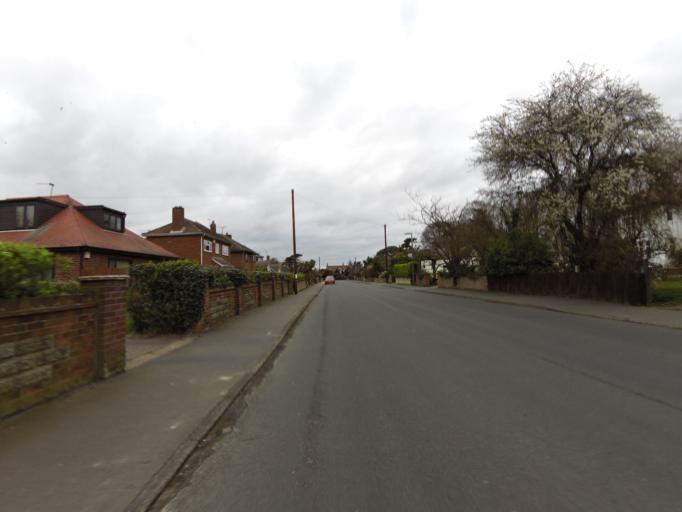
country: GB
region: England
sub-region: Norfolk
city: Hopton on Sea
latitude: 52.5119
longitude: 1.7436
